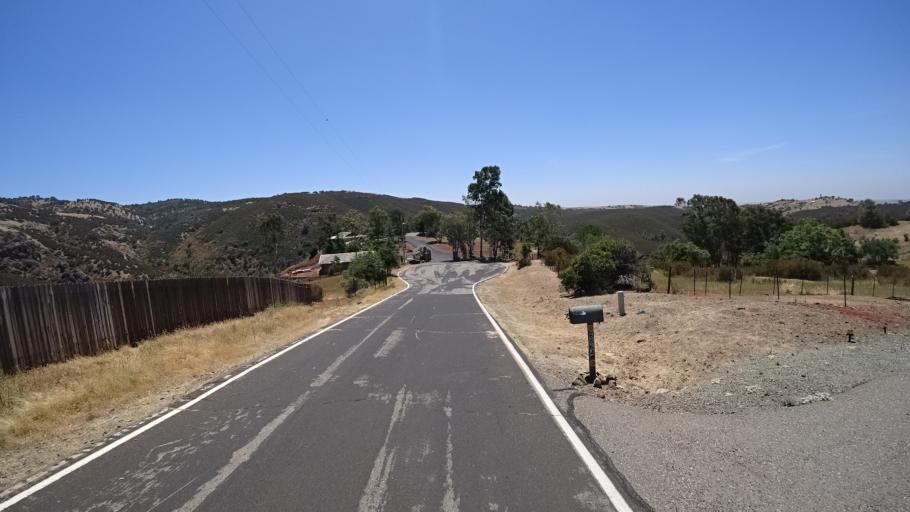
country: US
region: California
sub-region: Calaveras County
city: Rancho Calaveras
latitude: 38.1168
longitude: -120.8410
